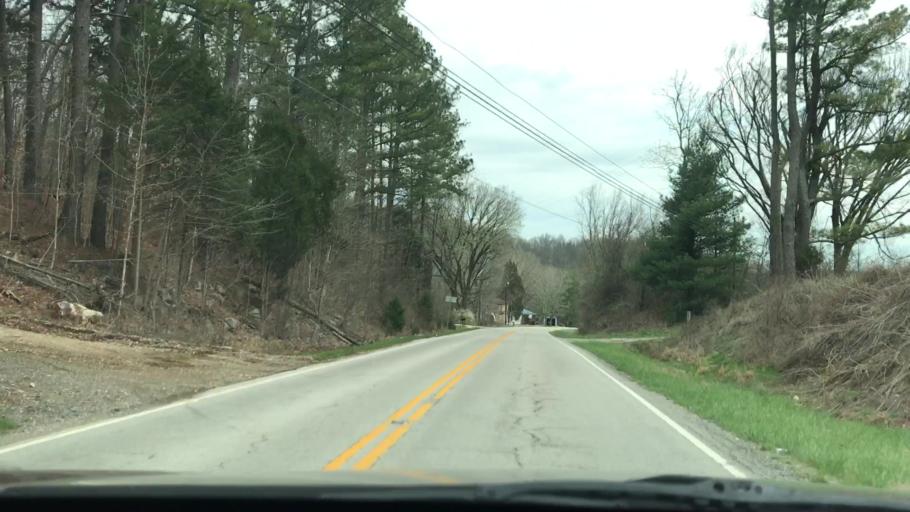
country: US
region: Kentucky
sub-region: Hart County
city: Munfordville
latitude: 37.3283
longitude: -85.7645
